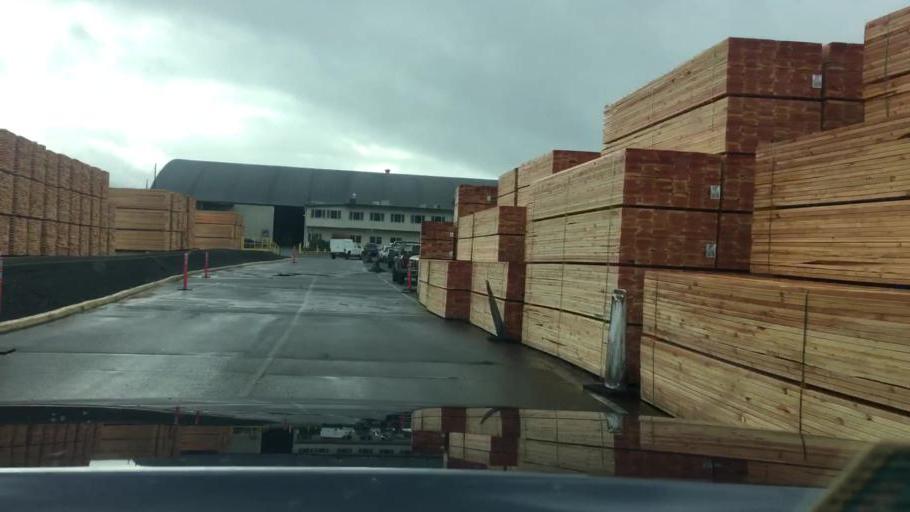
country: US
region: Oregon
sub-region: Lane County
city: Cottage Grove
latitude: 43.7675
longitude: -123.0792
